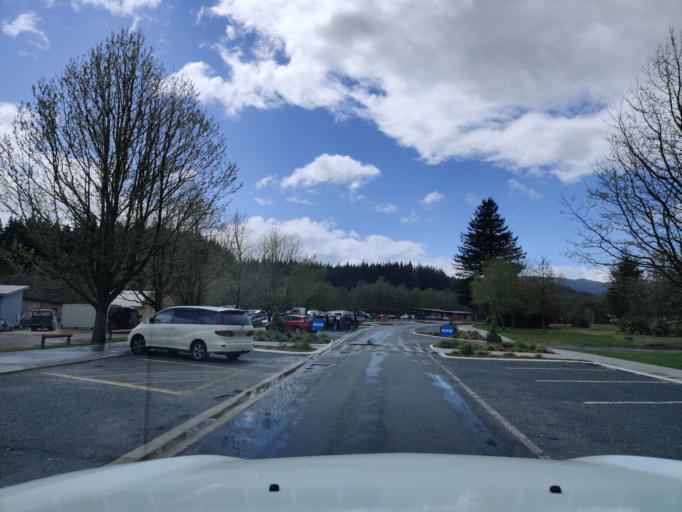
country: NZ
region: Bay of Plenty
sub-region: Rotorua District
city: Rotorua
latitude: -38.1761
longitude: 176.2508
